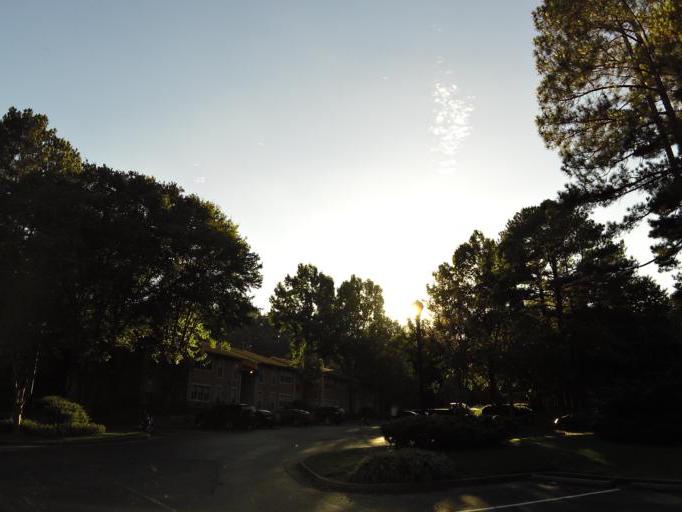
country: US
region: Georgia
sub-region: Cobb County
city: Vinings
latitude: 33.9068
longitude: -84.4501
